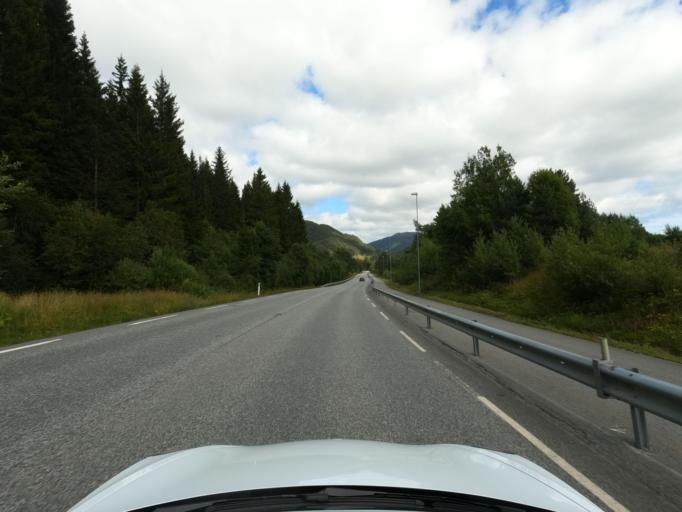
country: NO
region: Hordaland
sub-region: Os
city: Hagavik
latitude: 60.1933
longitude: 5.4211
